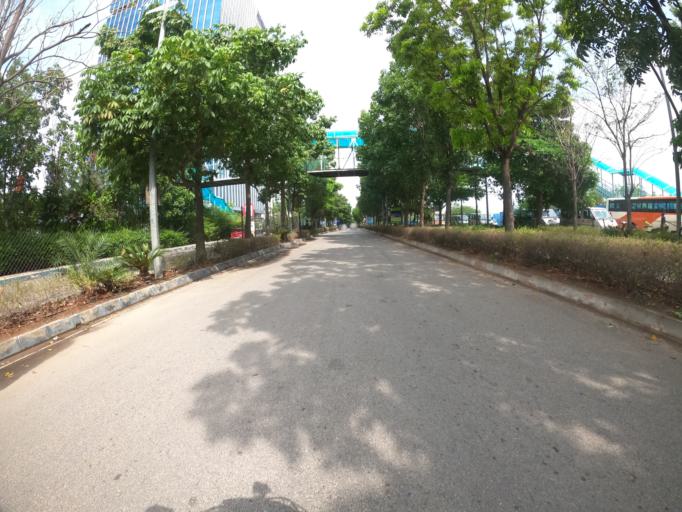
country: IN
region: Telangana
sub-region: Rangareddi
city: Kukatpalli
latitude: 17.4118
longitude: 78.3697
